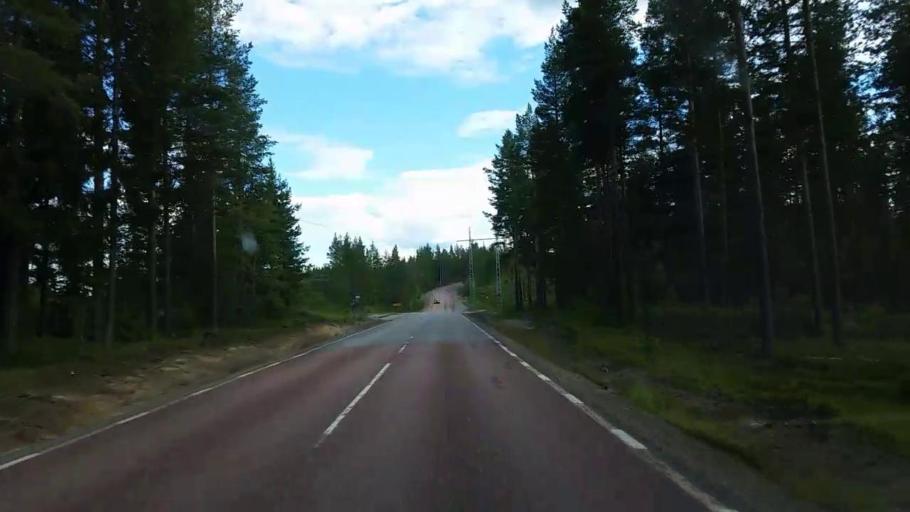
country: SE
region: Gaevleborg
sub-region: Ljusdals Kommun
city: Farila
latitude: 62.0161
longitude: 15.9073
